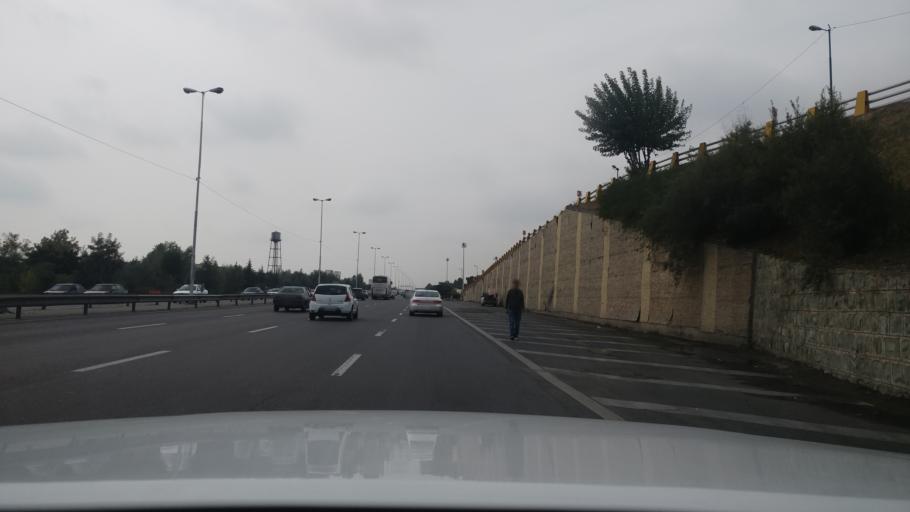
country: IR
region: Tehran
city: Tehran
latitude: 35.7162
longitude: 51.2857
